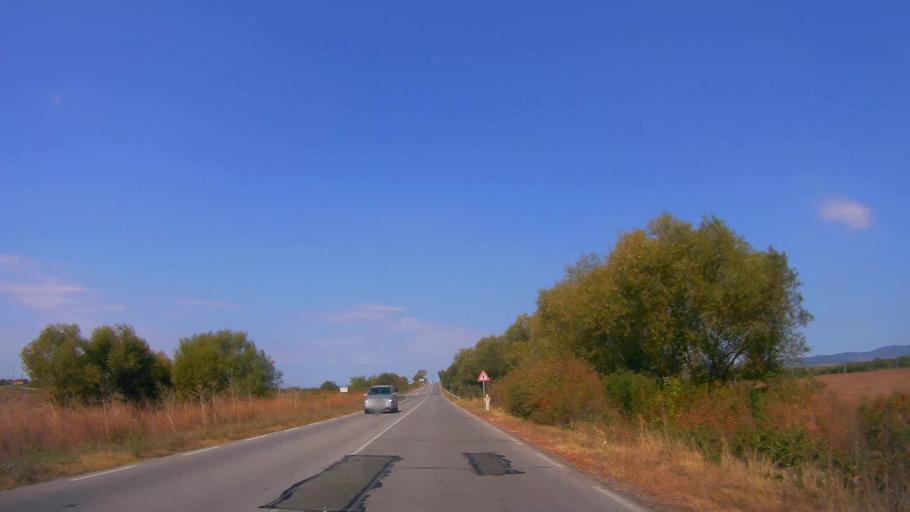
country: BG
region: Burgas
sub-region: Obshtina Karnobat
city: Karnobat
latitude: 42.6732
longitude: 26.9954
